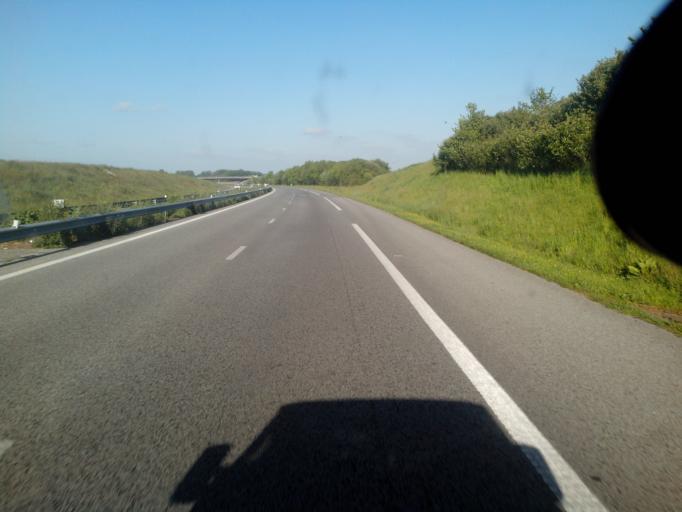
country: FR
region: Haute-Normandie
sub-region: Departement de la Seine-Maritime
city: Fauville-en-Caux
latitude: 49.6203
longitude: 0.5837
